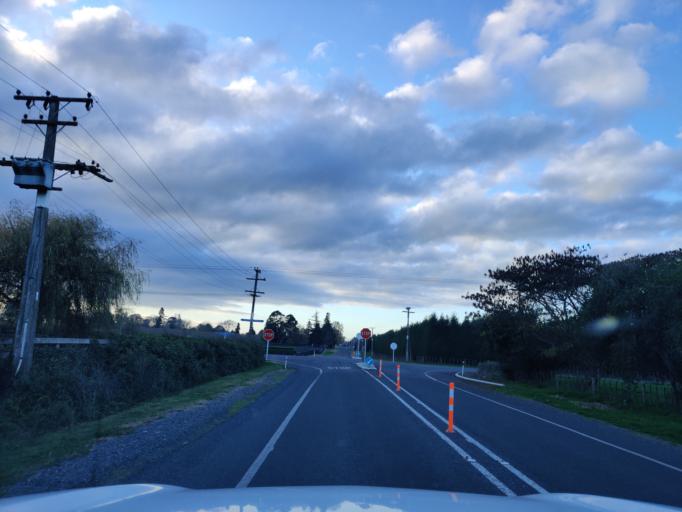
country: NZ
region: Waikato
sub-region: Waipa District
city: Cambridge
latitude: -37.8607
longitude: 175.4390
